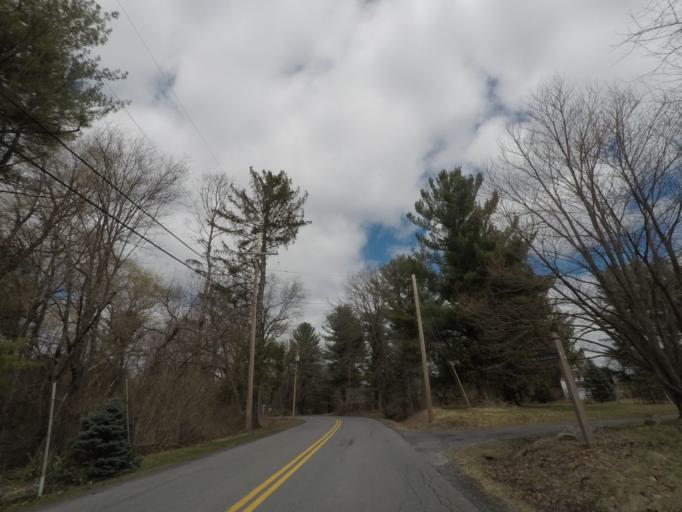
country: US
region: New York
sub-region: Albany County
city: Voorheesville
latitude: 42.6303
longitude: -73.8833
